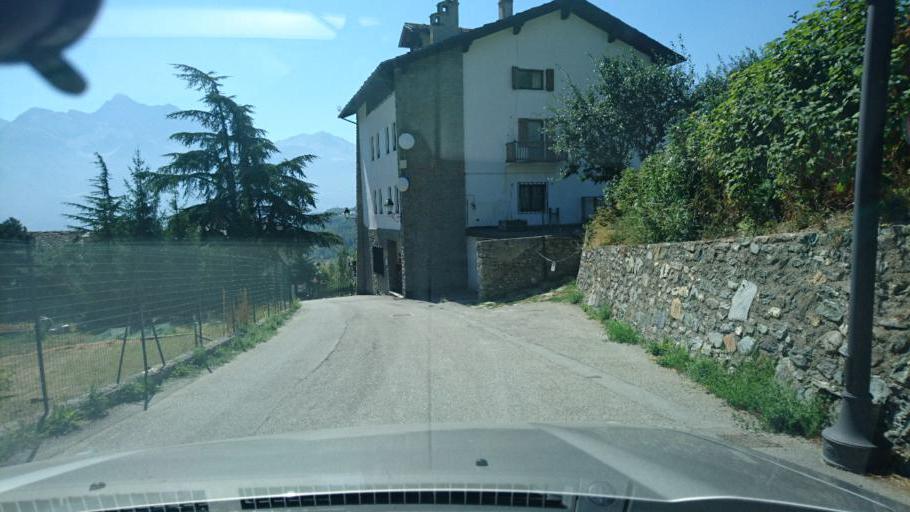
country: IT
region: Aosta Valley
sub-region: Valle d'Aosta
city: Gignod
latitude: 45.7824
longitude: 7.2968
